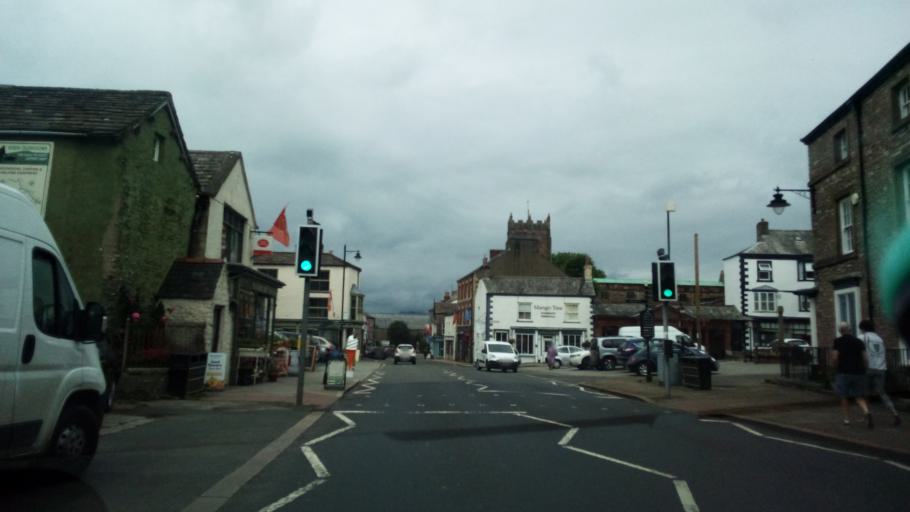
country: GB
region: England
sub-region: Cumbria
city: Kirkby Stephen
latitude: 54.4730
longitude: -2.3487
